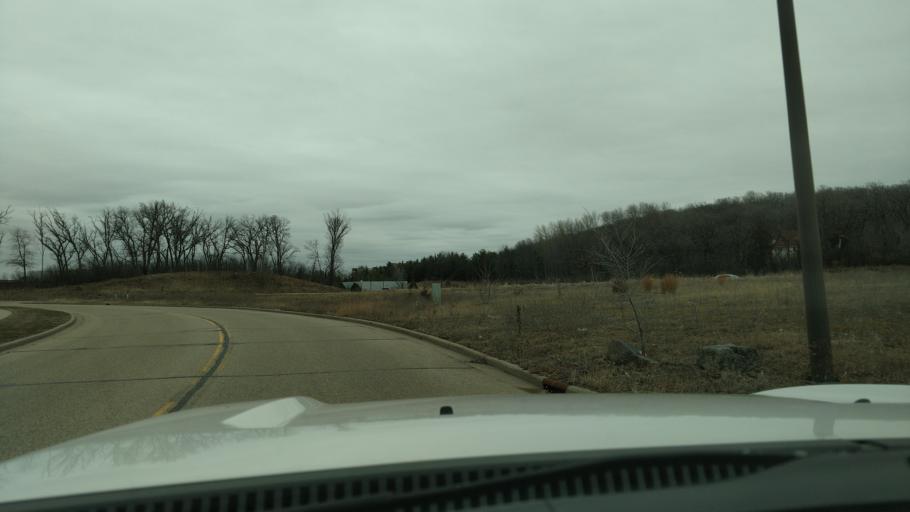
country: US
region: Wisconsin
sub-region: Saint Croix County
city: Hudson
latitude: 44.9588
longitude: -92.7182
